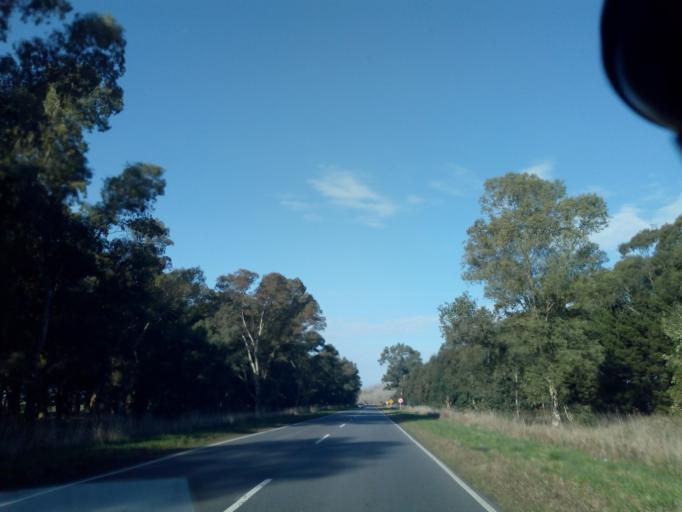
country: AR
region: Buenos Aires
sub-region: Partido de Tandil
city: Tandil
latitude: -37.3558
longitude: -58.8748
